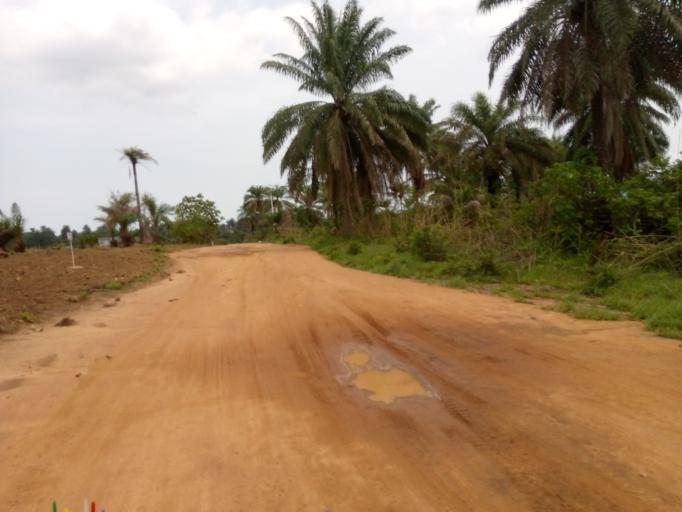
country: SL
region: Western Area
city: Waterloo
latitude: 8.3436
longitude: -13.0148
